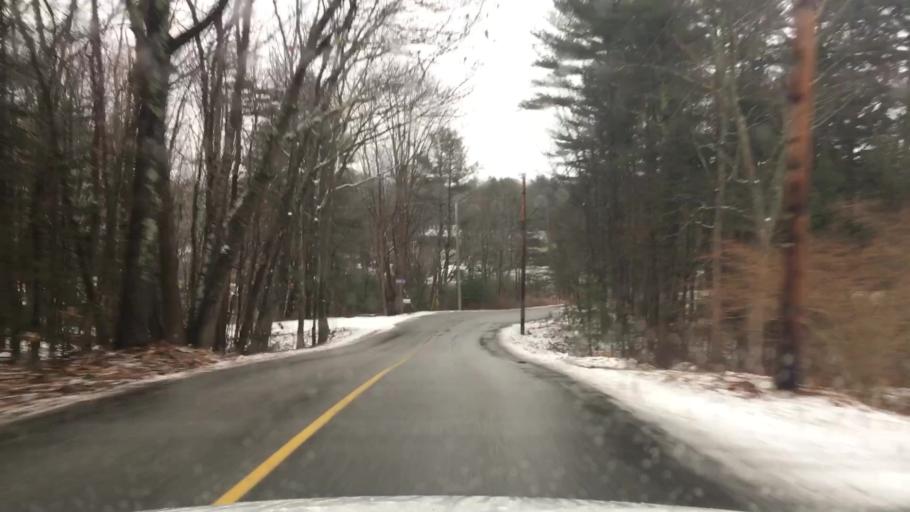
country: US
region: Maine
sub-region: York County
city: Arundel
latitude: 43.3752
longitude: -70.4589
